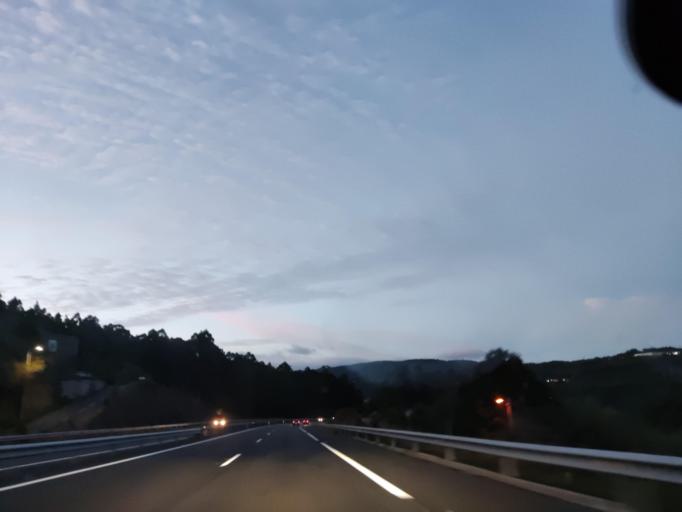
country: ES
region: Galicia
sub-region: Provincia da Coruna
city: Boiro
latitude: 42.6518
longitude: -8.9019
